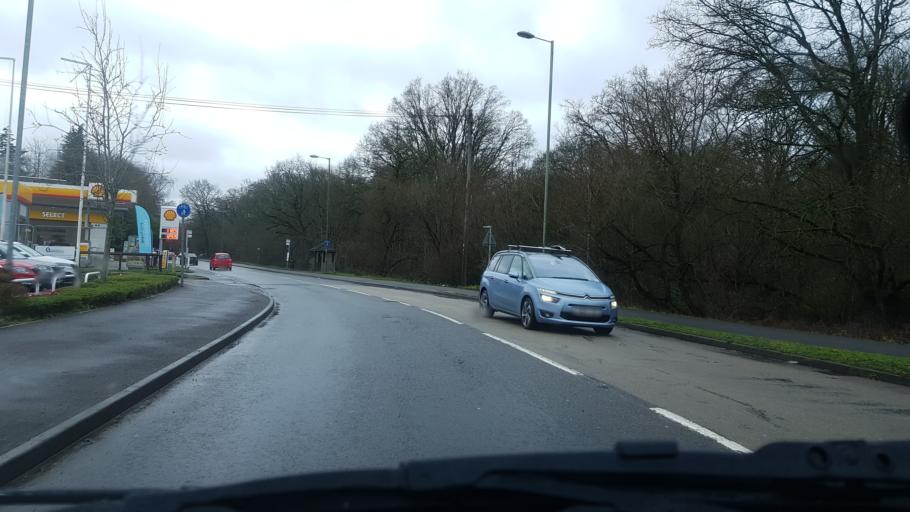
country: GB
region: England
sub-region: Surrey
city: Shalford
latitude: 51.2063
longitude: -0.5852
